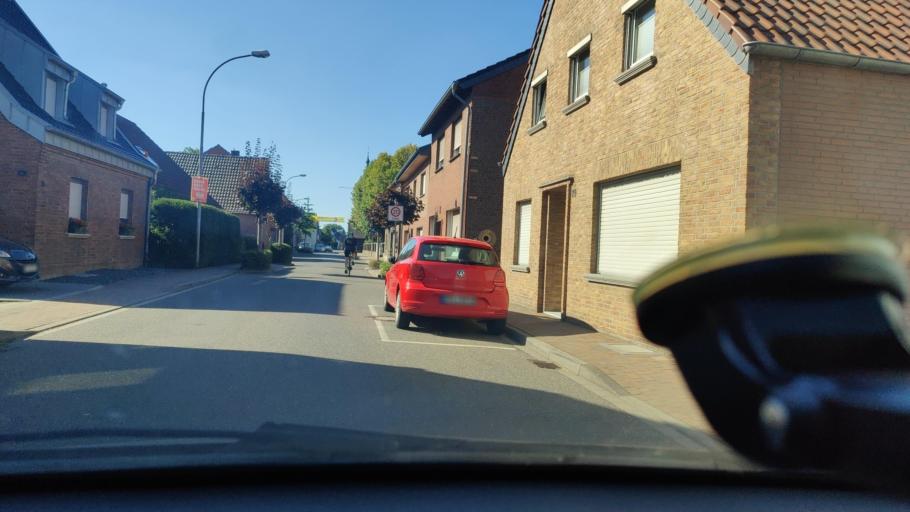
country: DE
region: North Rhine-Westphalia
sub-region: Regierungsbezirk Dusseldorf
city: Wachtendonk
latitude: 51.4536
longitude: 6.3759
